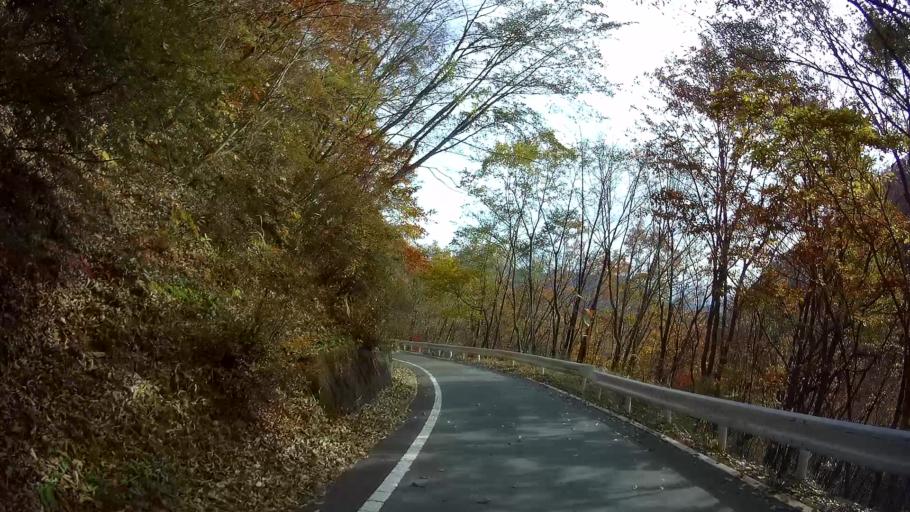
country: JP
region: Gunma
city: Nakanojomachi
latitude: 36.6350
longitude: 138.6459
